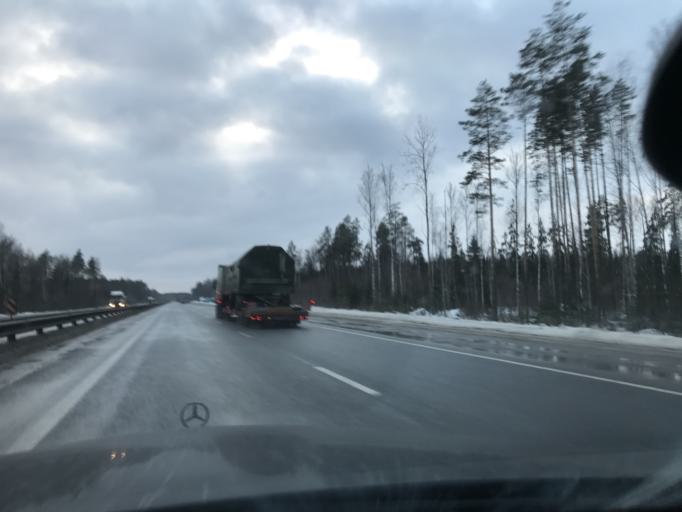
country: RU
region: Vladimir
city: Kameshkovo
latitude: 56.1602
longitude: 40.9281
